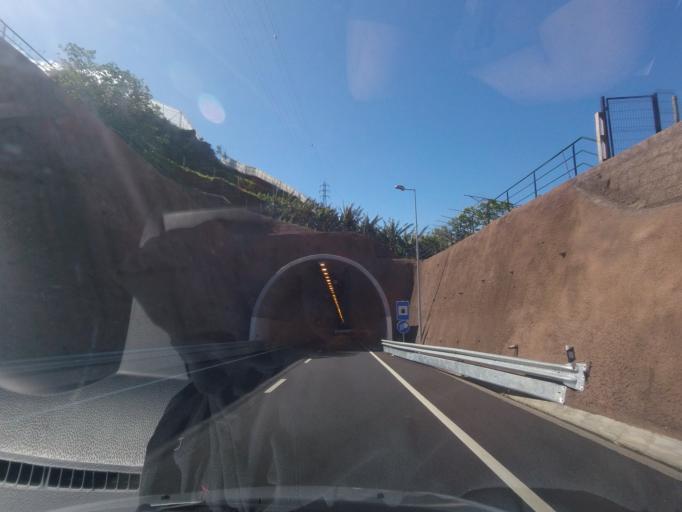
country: PT
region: Madeira
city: Camara de Lobos
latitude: 32.6663
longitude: -16.9699
